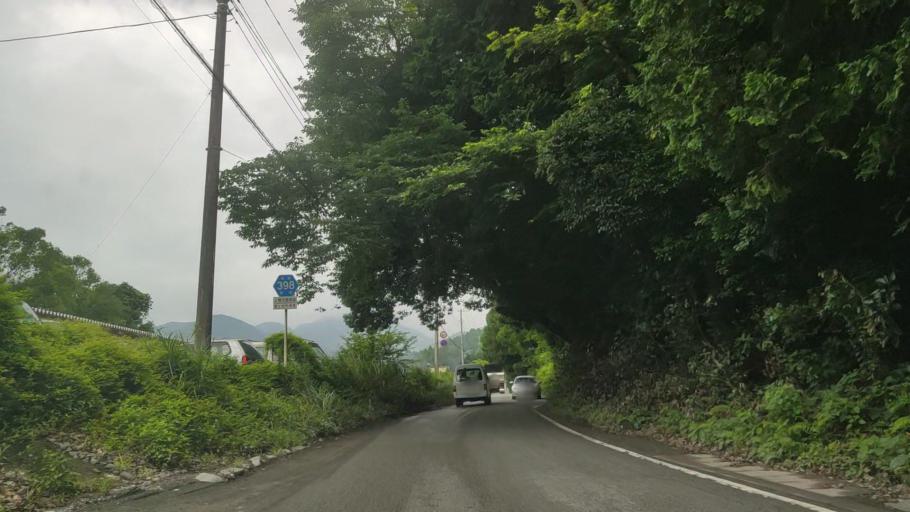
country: JP
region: Shizuoka
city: Fujinomiya
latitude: 35.2154
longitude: 138.5444
